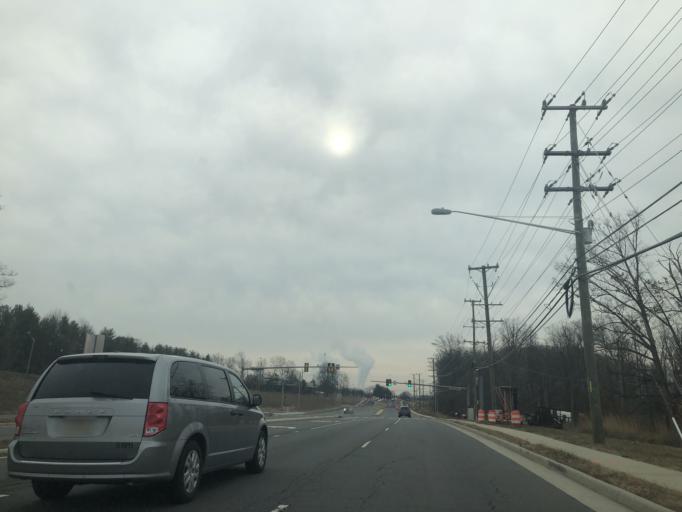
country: US
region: Virginia
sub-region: Loudoun County
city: Leesburg
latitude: 39.0879
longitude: -77.5535
